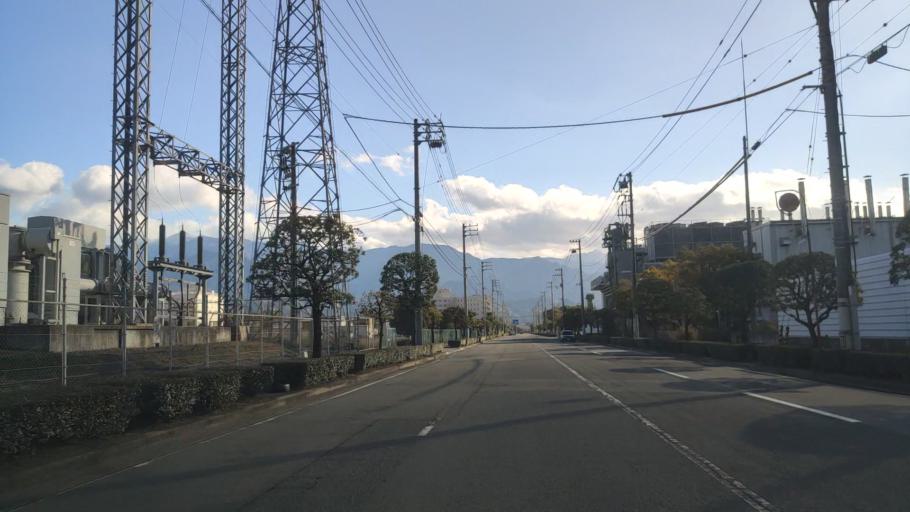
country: JP
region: Ehime
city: Saijo
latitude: 33.9390
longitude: 133.1916
